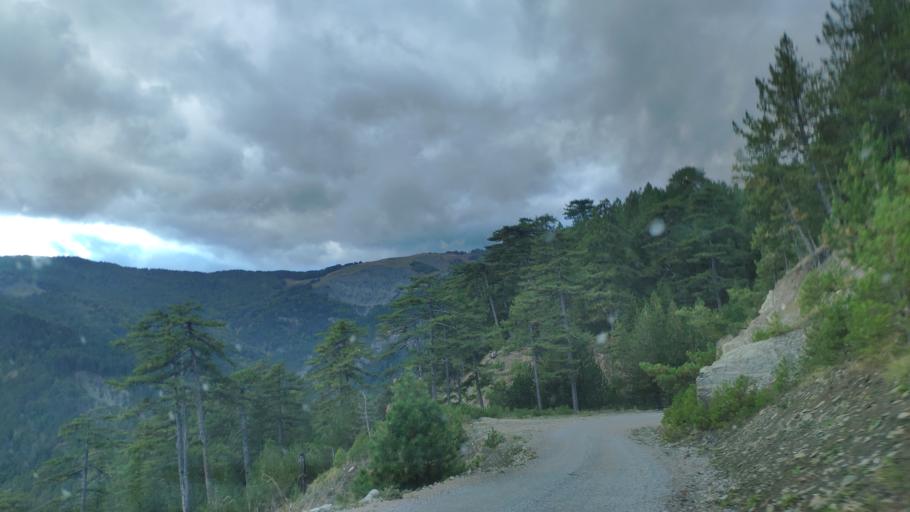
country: AL
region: Korce
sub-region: Rrethi i Kolonjes
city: Erseke
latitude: 40.2901
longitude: 20.8608
